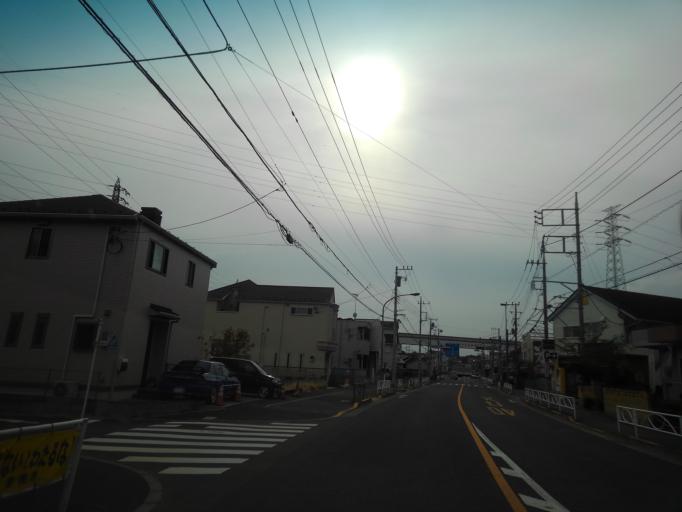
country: JP
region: Tokyo
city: Hino
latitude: 35.6797
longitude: 139.4099
